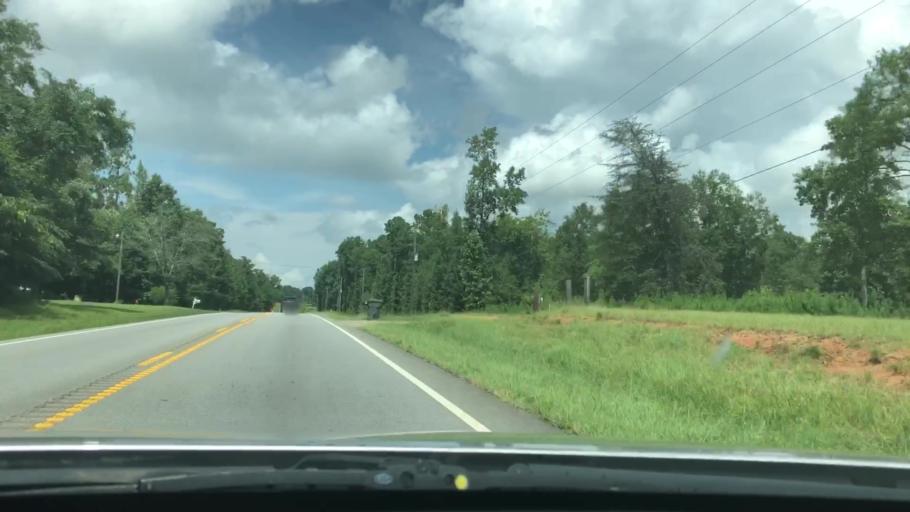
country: US
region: Georgia
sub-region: Lamar County
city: Barnesville
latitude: 33.1248
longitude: -84.1539
